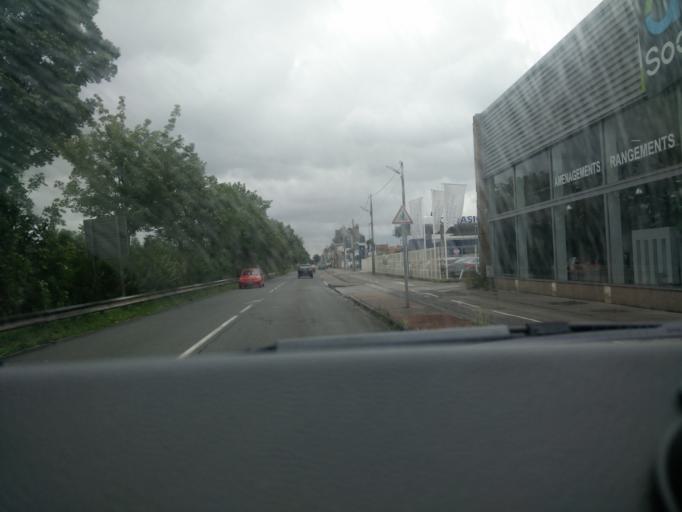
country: FR
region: Nord-Pas-de-Calais
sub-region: Departement du Nord
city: Dunkerque
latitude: 51.0223
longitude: 2.3748
